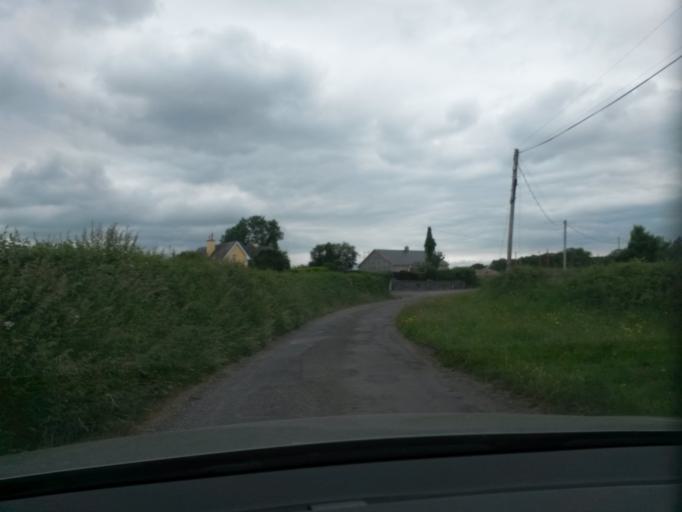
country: IE
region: Munster
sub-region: An Clar
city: Ennis
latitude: 52.9134
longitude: -9.0540
